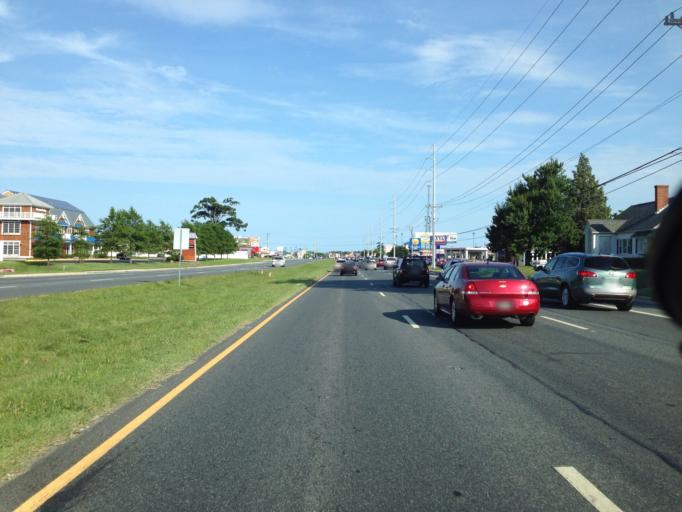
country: US
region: Delaware
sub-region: Sussex County
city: Lewes
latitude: 38.7270
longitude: -75.1279
